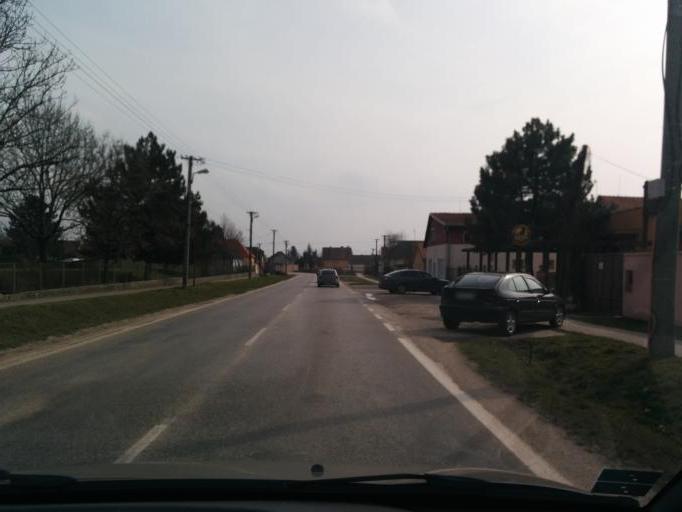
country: SK
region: Trnavsky
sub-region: Okres Galanta
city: Galanta
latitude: 48.2519
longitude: 17.8165
